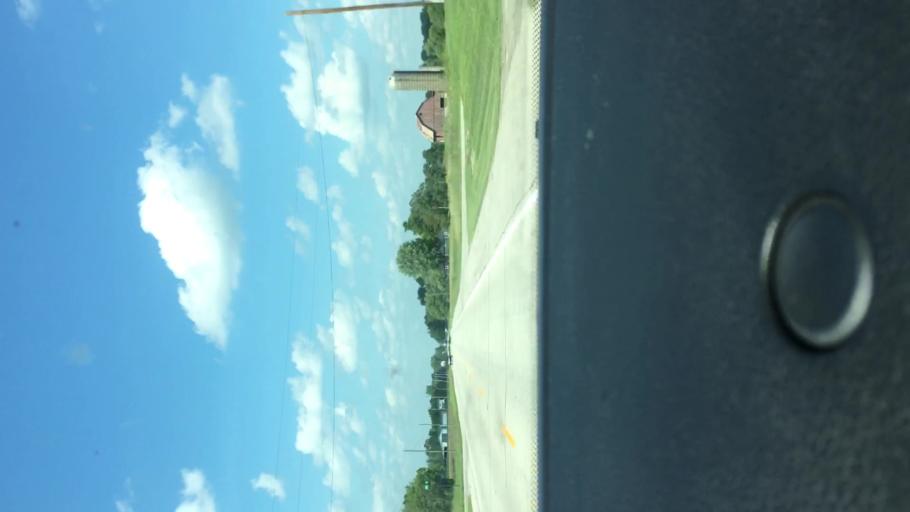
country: US
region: Indiana
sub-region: Randolph County
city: Winchester
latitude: 40.2580
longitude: -84.9762
